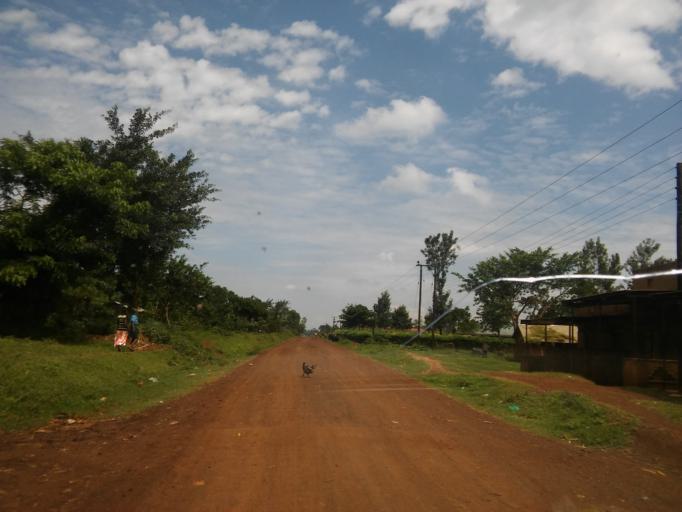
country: UG
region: Eastern Region
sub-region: Bududa District
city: Bududa
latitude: 0.8913
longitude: 34.2634
